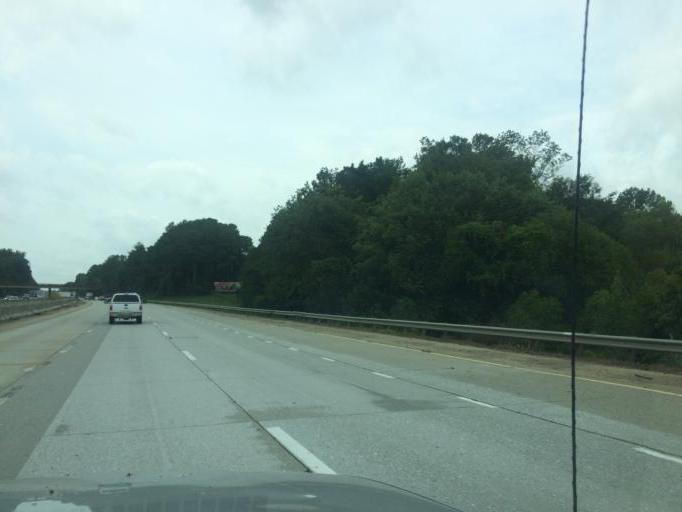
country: US
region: South Carolina
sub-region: Anderson County
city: Northlake
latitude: 34.5983
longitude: -82.6586
